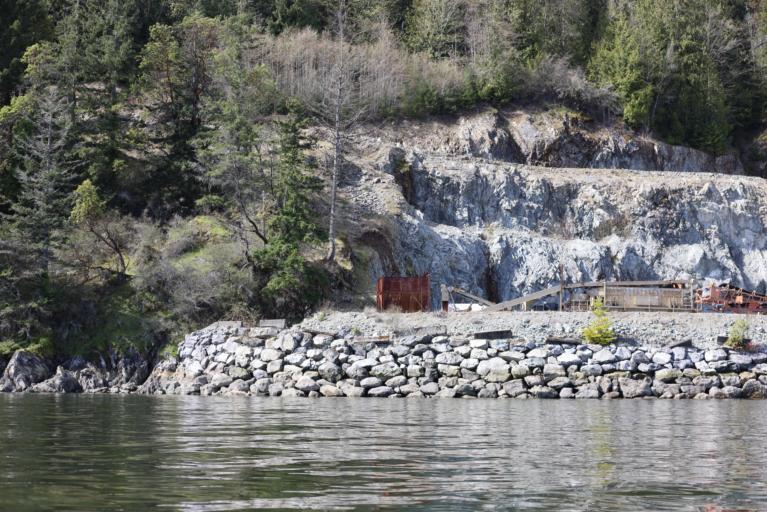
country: CA
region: British Columbia
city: North Saanich
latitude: 48.5819
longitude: -123.5200
